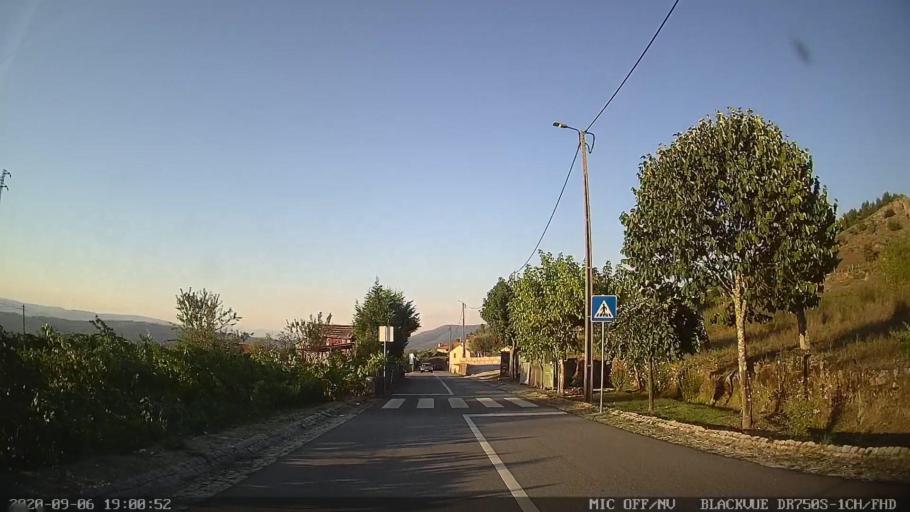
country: PT
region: Porto
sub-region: Baiao
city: Baiao
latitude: 41.2373
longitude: -7.9984
